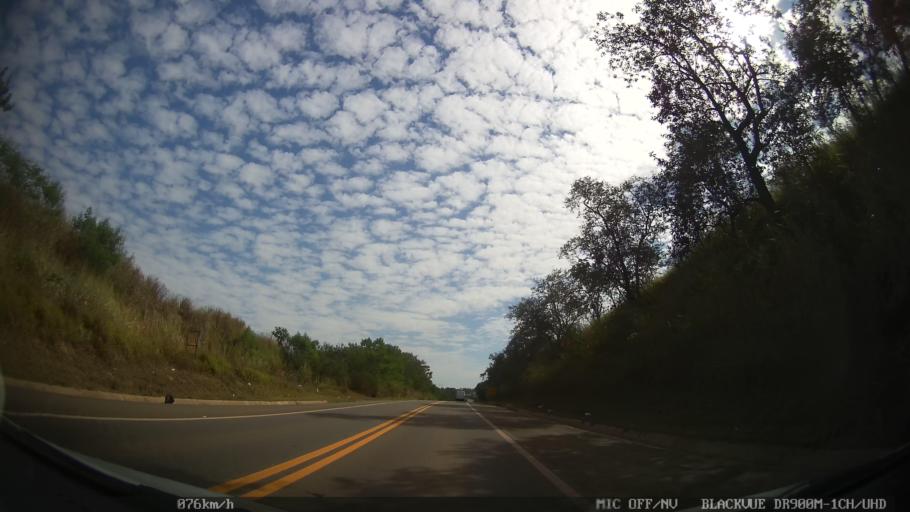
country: BR
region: Sao Paulo
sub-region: Santa Barbara D'Oeste
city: Santa Barbara d'Oeste
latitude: -22.7072
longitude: -47.4388
